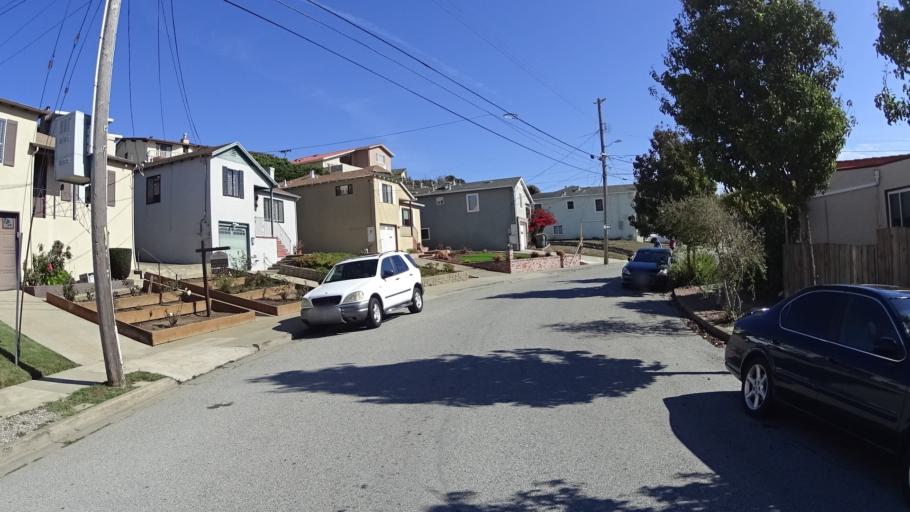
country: US
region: California
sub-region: San Mateo County
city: South San Francisco
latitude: 37.6611
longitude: -122.4172
